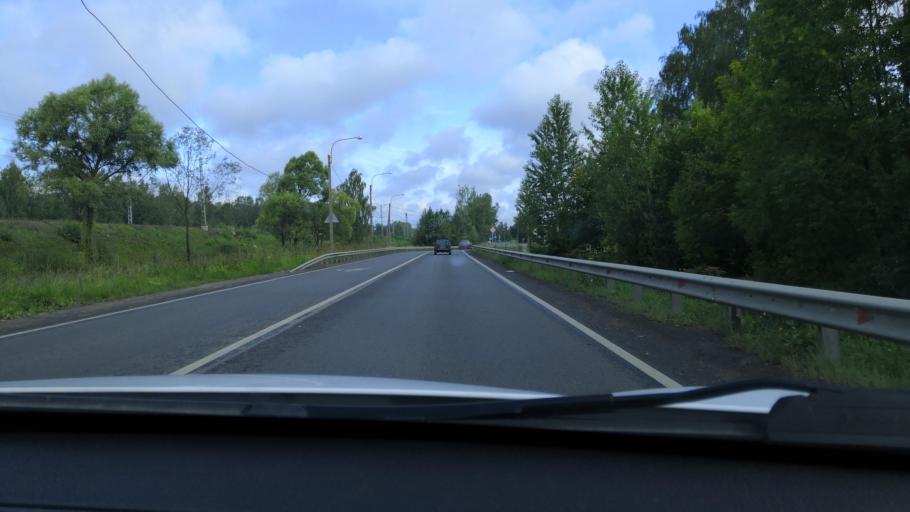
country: RU
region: St.-Petersburg
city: Tyarlevo
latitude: 59.7039
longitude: 30.4391
